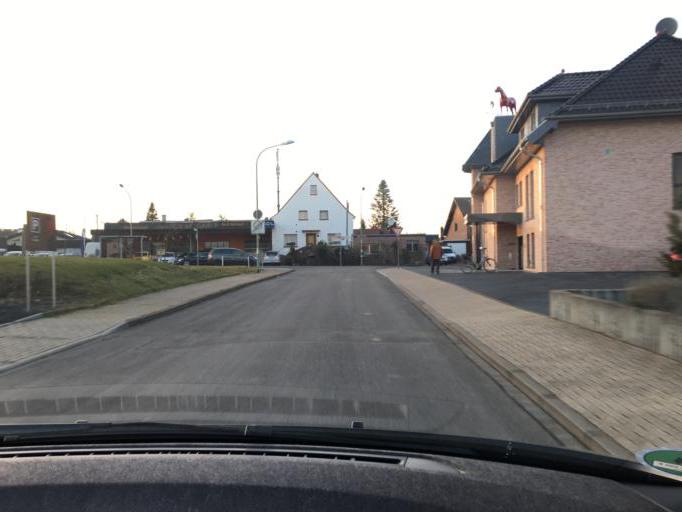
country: DE
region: North Rhine-Westphalia
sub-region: Regierungsbezirk Koln
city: Kreuzau
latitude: 50.7680
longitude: 6.4480
